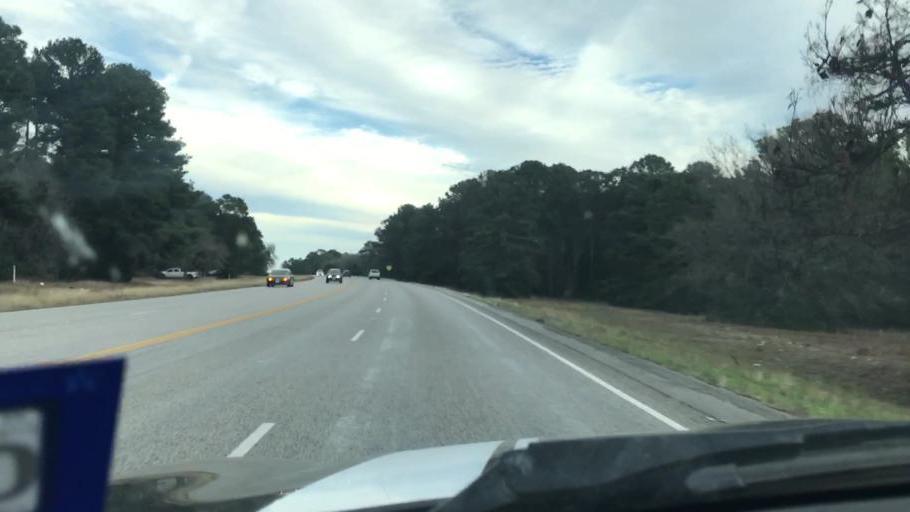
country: US
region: Texas
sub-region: Bastrop County
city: Camp Swift
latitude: 30.2419
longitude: -97.2139
